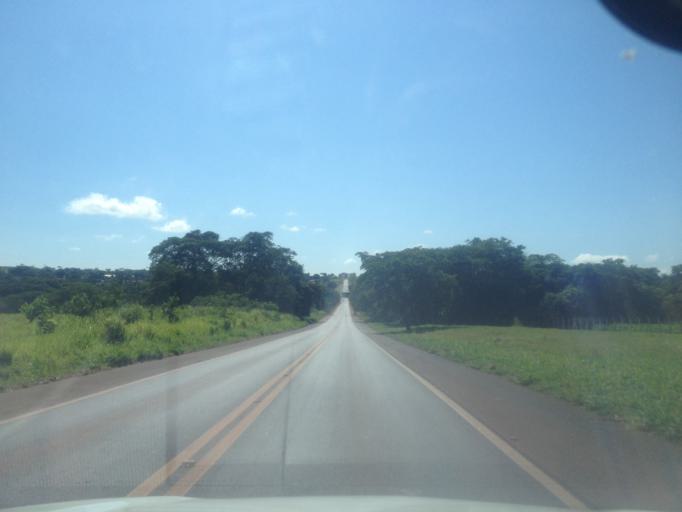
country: BR
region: Minas Gerais
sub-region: Santa Vitoria
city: Santa Vitoria
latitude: -19.0427
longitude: -50.5059
